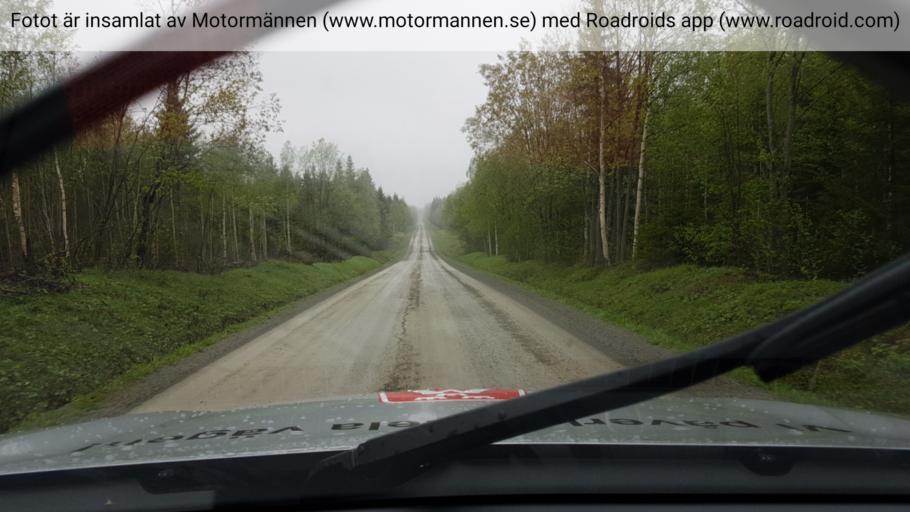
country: SE
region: Jaemtland
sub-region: Bergs Kommun
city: Hoverberg
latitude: 62.9639
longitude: 14.2349
